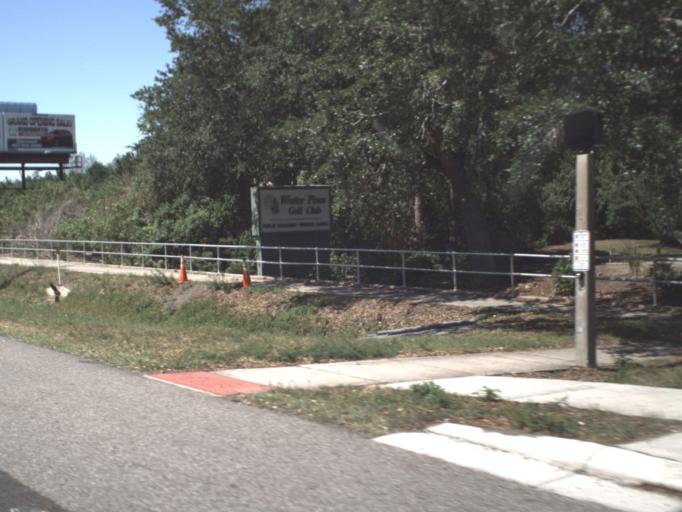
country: US
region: Florida
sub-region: Orange County
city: Union Park
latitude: 28.5792
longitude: -81.3090
